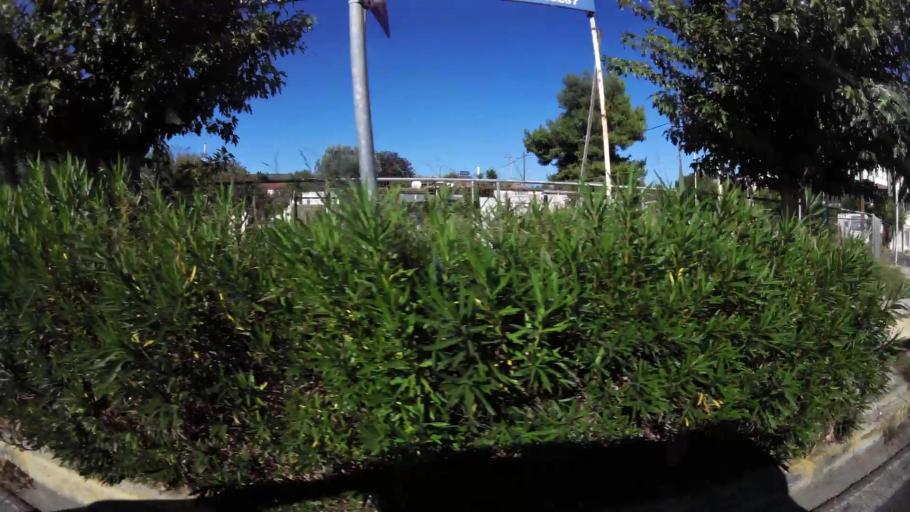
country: GR
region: Attica
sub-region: Nomarchia Anatolikis Attikis
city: Pallini
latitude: 38.0037
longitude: 23.8967
